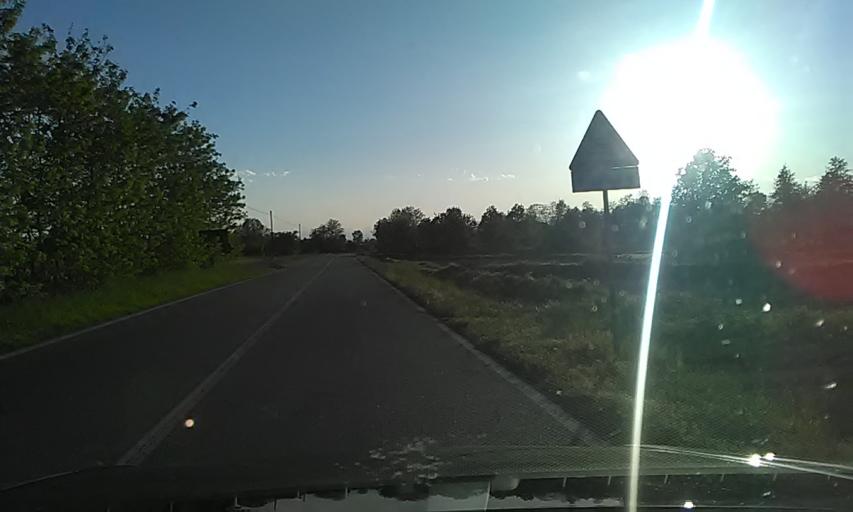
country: IT
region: Piedmont
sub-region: Provincia di Vercelli
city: Ghislarengo
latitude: 45.5247
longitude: 8.3786
